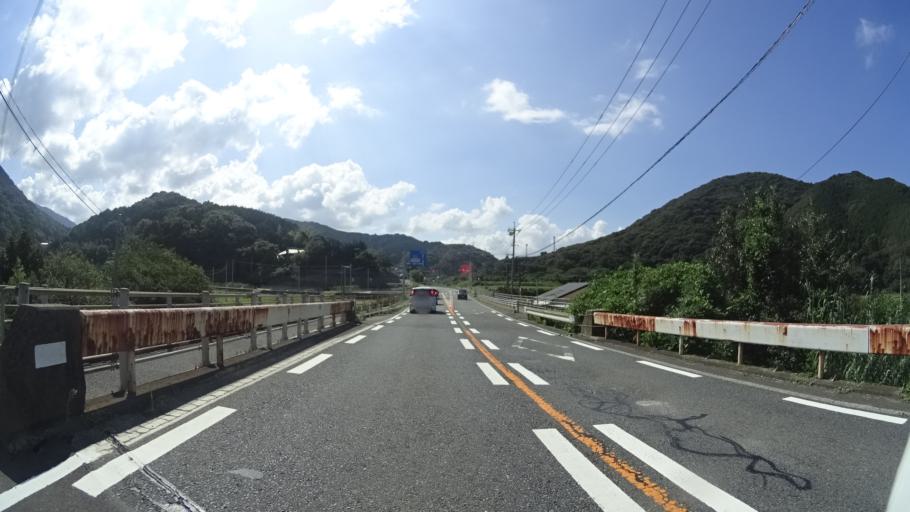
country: JP
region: Yamaguchi
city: Shimonoseki
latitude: 34.2258
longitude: 130.9296
